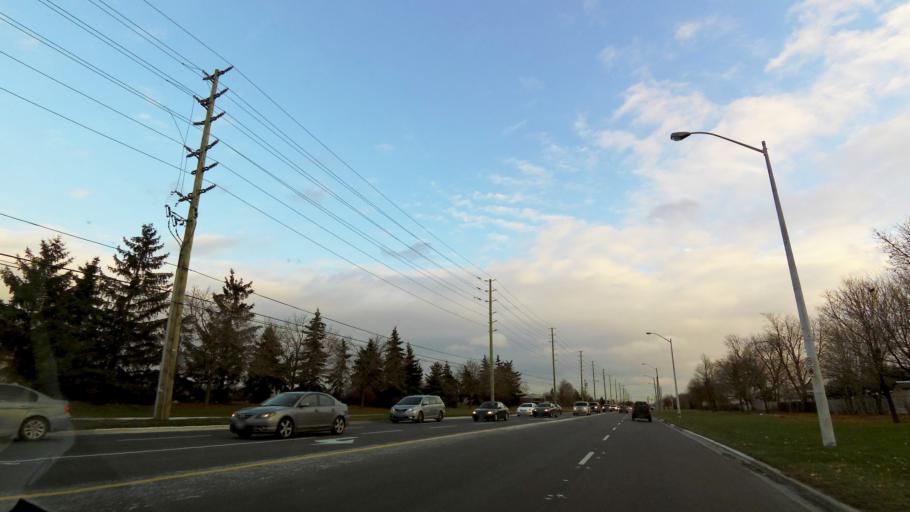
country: CA
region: Ontario
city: Brampton
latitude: 43.7382
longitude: -79.7125
